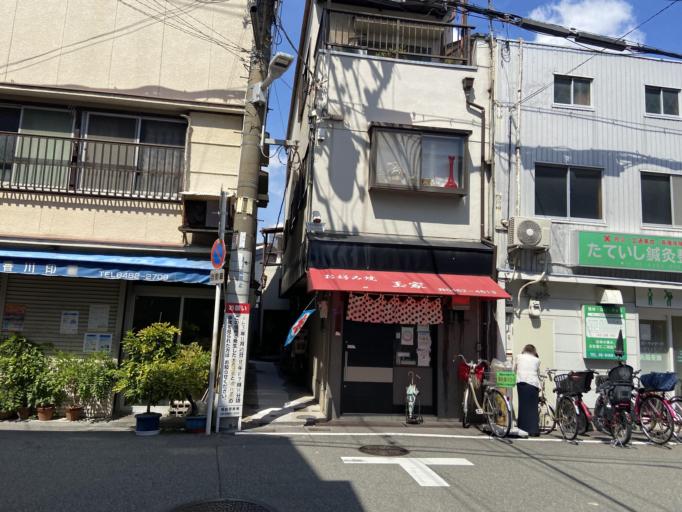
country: JP
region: Osaka
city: Osaka-shi
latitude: 34.6856
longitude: 135.4745
